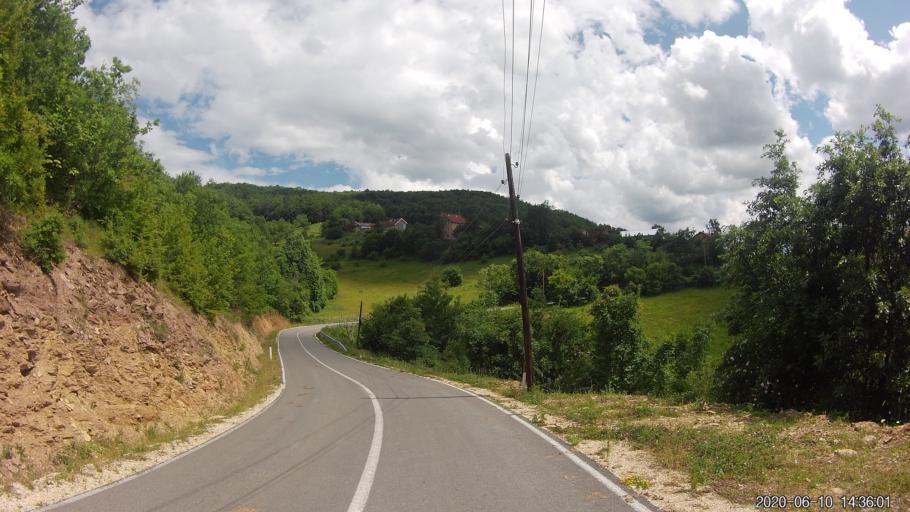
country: XK
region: Prizren
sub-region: Komuna e Therandes
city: Budakovo
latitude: 42.4120
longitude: 20.9358
